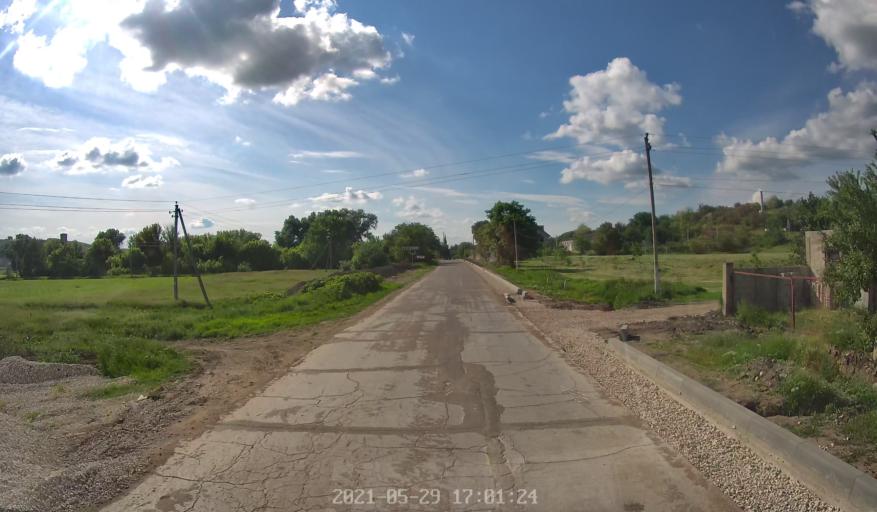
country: MD
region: Laloveni
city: Ialoveni
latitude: 46.8316
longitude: 28.8591
